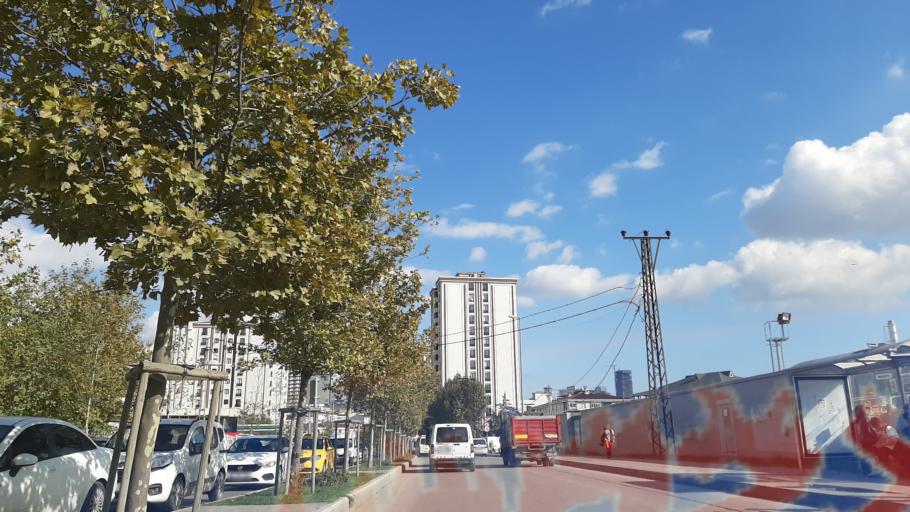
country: TR
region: Istanbul
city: Esenyurt
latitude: 41.0307
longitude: 28.6609
